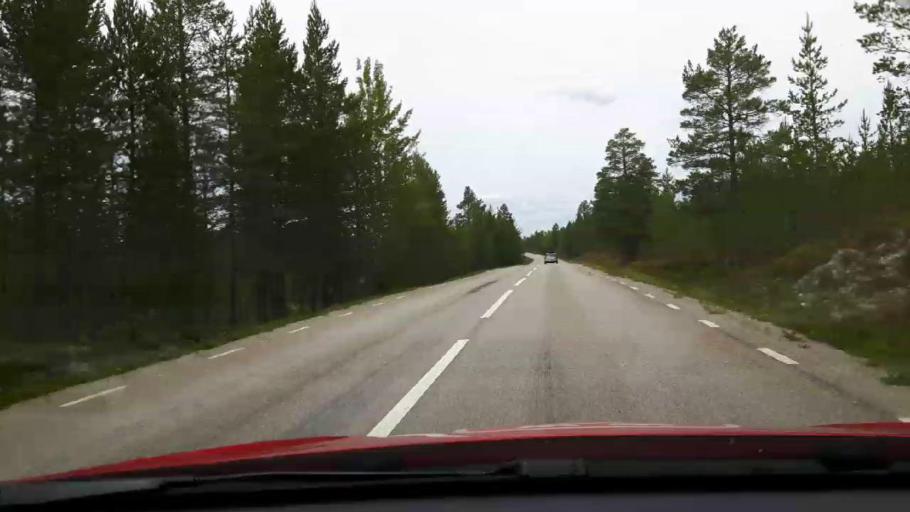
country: SE
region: Jaemtland
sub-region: Harjedalens Kommun
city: Sveg
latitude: 62.2347
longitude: 13.8538
